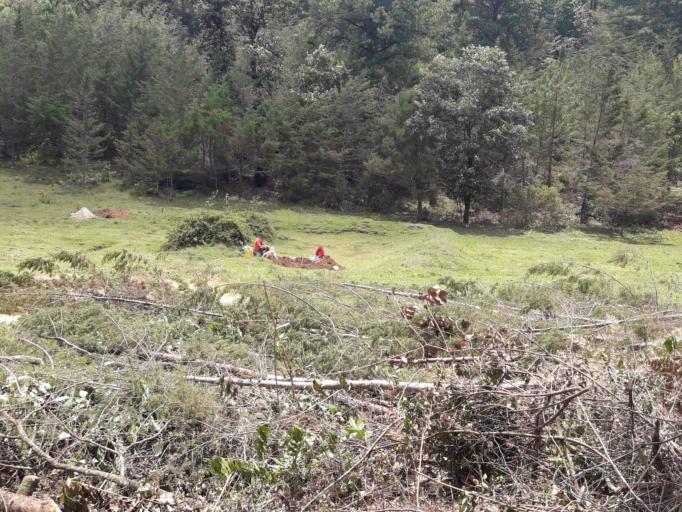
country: GT
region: Quiche
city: Nebaj
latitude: 15.4283
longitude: -91.1361
